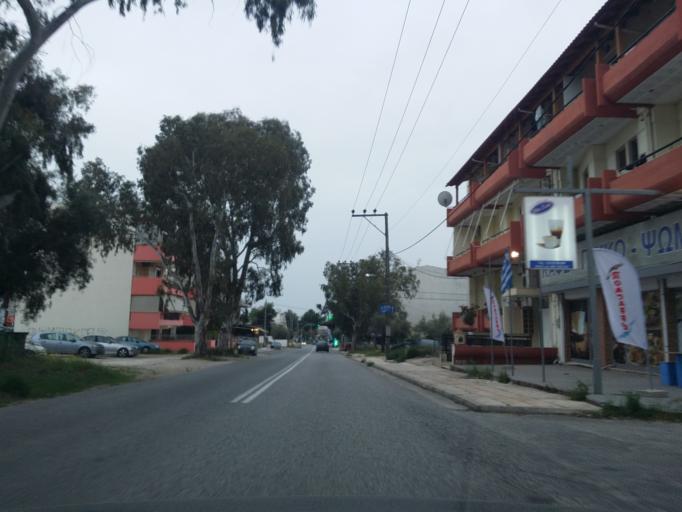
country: GR
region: Attica
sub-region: Nomarchia Dytikis Attikis
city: Mandra
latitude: 38.0811
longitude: 23.4932
